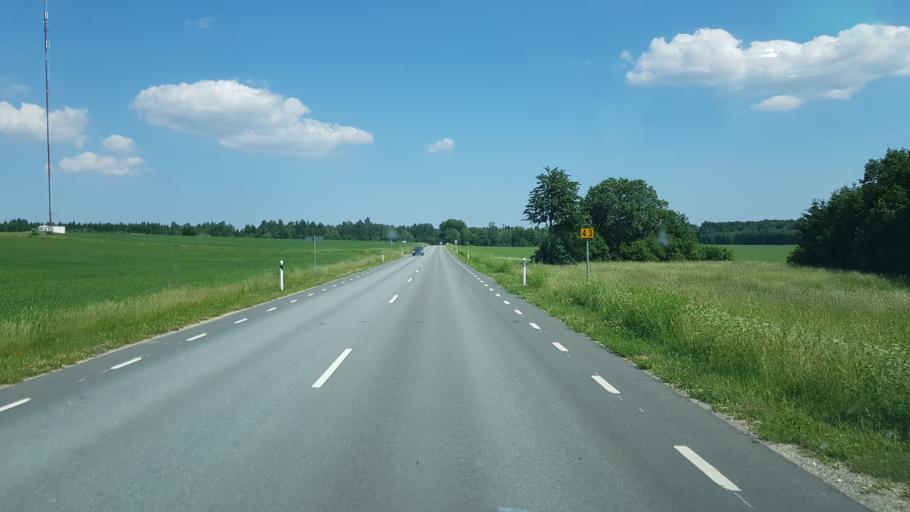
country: EE
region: Tartu
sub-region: Alatskivi vald
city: Kallaste
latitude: 58.5297
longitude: 27.0831
